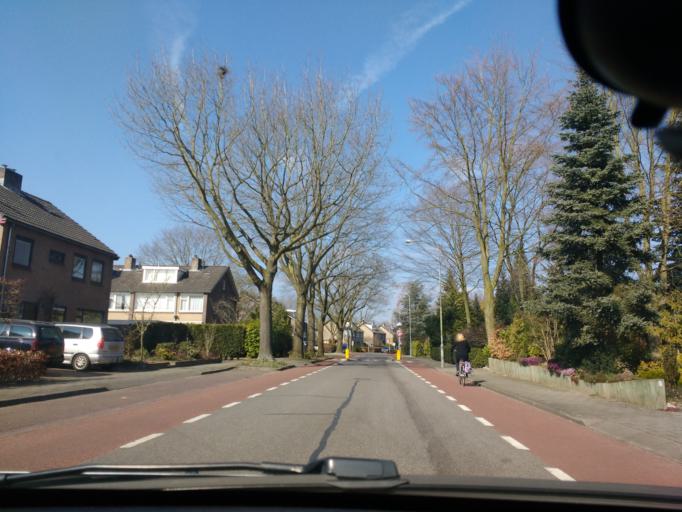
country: NL
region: Gelderland
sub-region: Gemeente Nijmegen
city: Nijmegen
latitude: 51.7868
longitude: 5.8573
